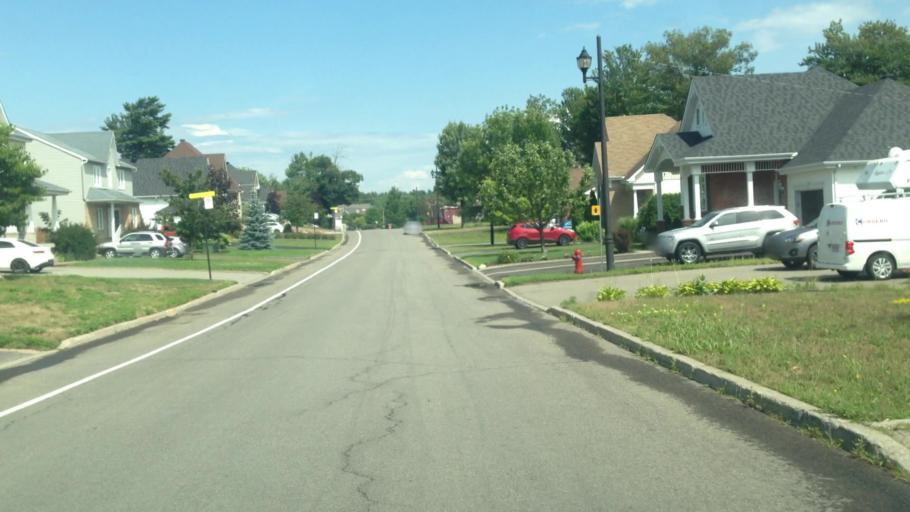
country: CA
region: Quebec
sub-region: Laurentides
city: Saint-Jerome
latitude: 45.8100
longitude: -74.0065
